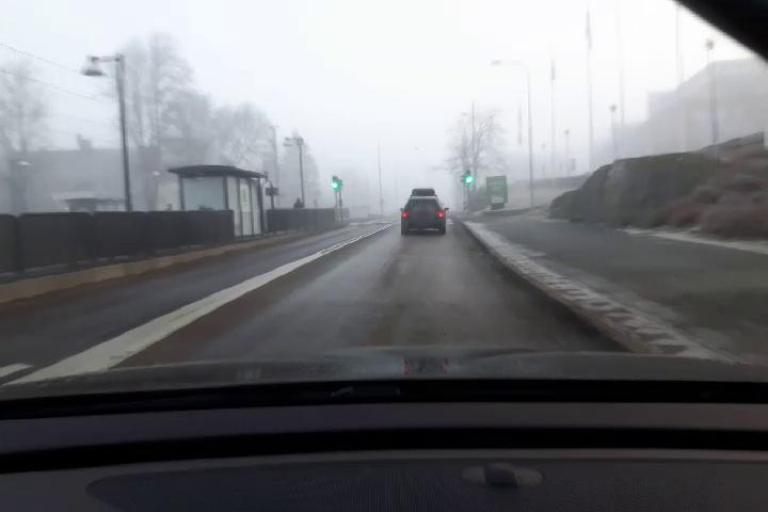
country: SE
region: Vaestra Goetaland
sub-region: Goteborg
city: Majorna
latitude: 57.6733
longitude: 11.8807
